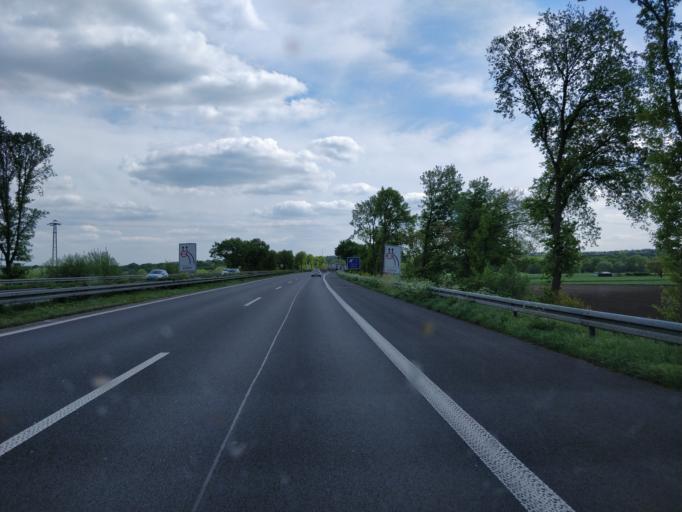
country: DE
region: North Rhine-Westphalia
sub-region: Regierungsbezirk Dusseldorf
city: Hunxe
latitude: 51.6518
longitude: 6.7354
